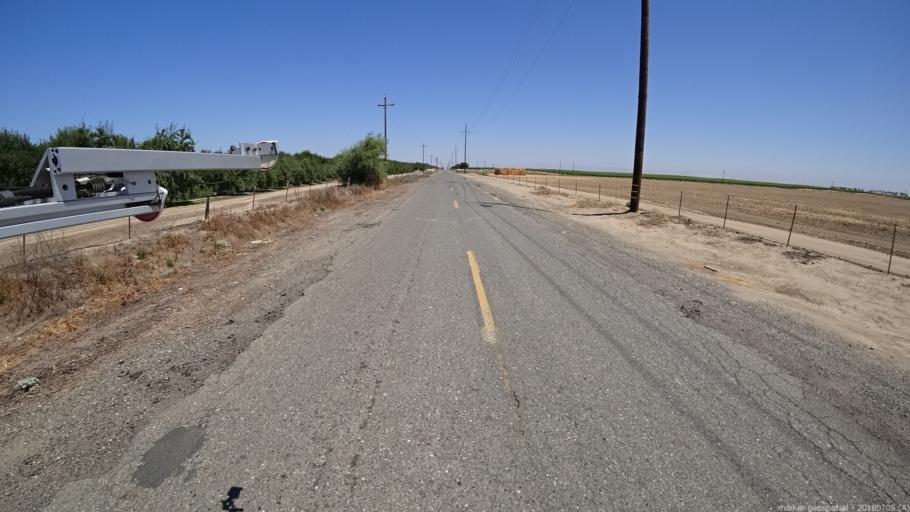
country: US
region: California
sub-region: Madera County
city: Chowchilla
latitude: 37.1627
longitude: -120.2020
